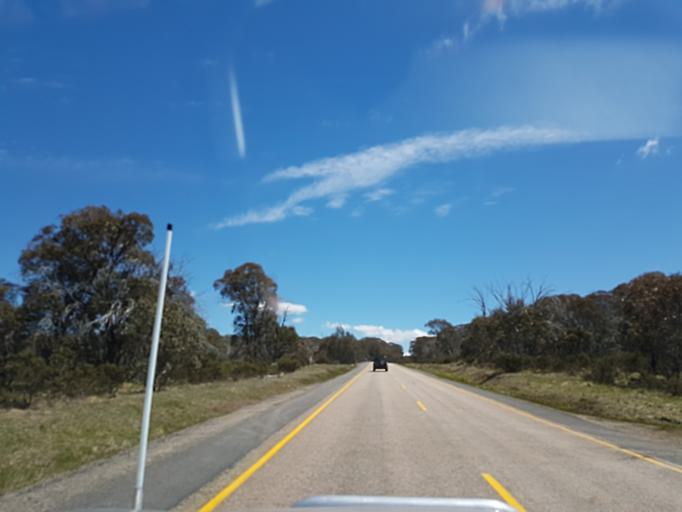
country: AU
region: Victoria
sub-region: Alpine
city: Mount Beauty
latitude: -37.0332
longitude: 147.3003
